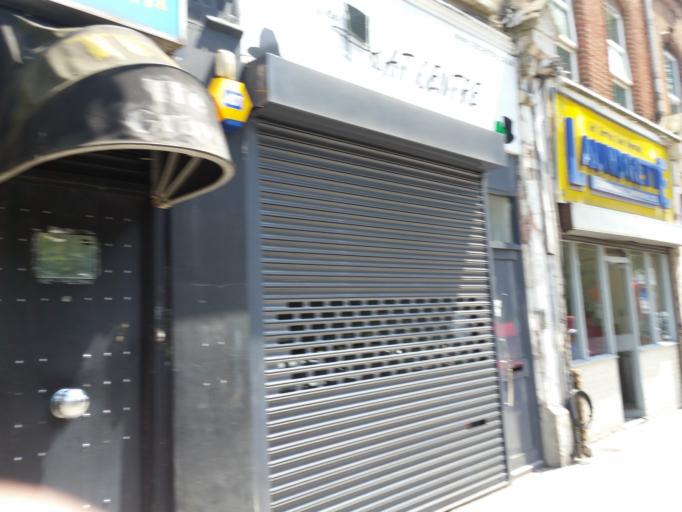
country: GB
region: England
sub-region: Greater London
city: Hackney
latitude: 51.5646
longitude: -0.0730
